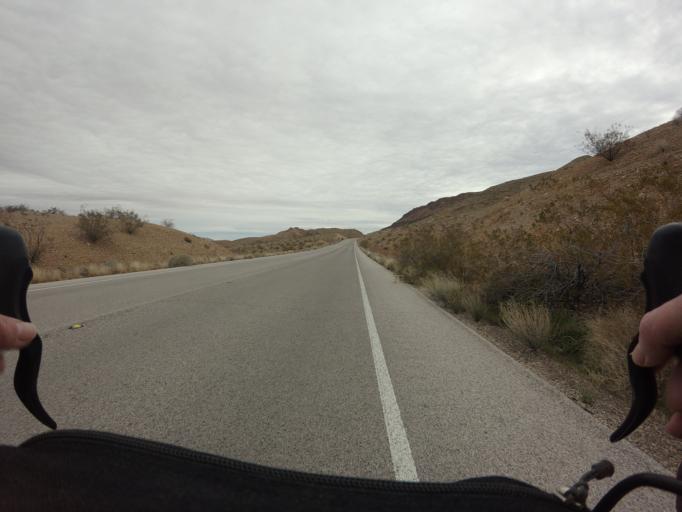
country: US
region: Nevada
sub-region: Clark County
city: Boulder City
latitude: 36.2307
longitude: -114.5754
